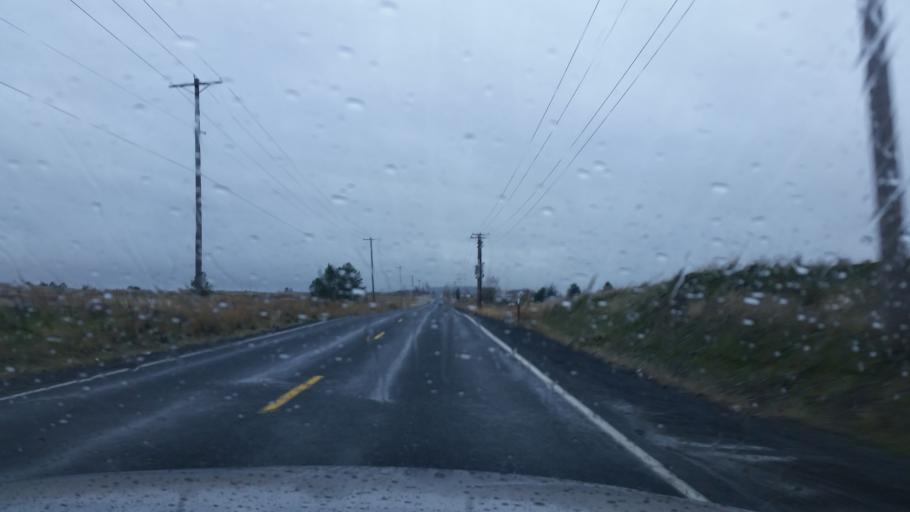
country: US
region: Washington
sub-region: Spokane County
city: Fairchild Air Force Base
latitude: 47.6020
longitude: -117.6075
